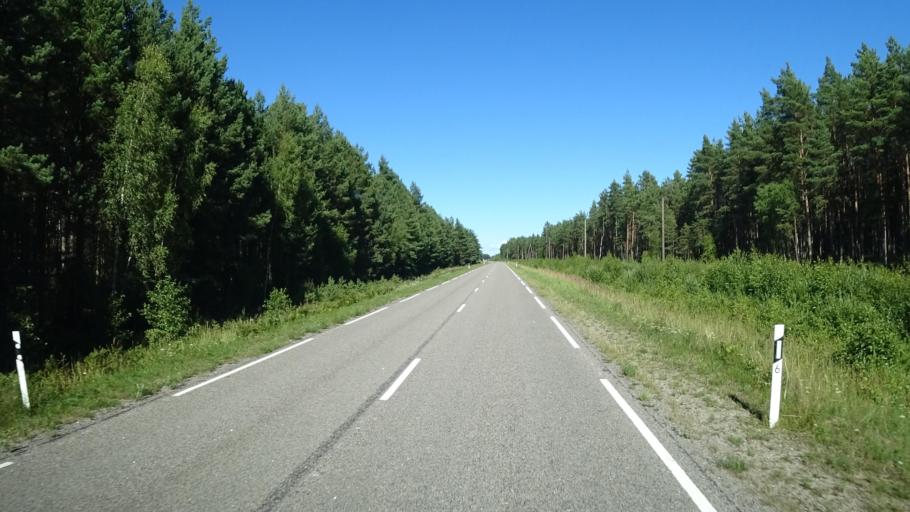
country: LV
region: Dundaga
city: Dundaga
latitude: 57.6912
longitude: 22.3878
